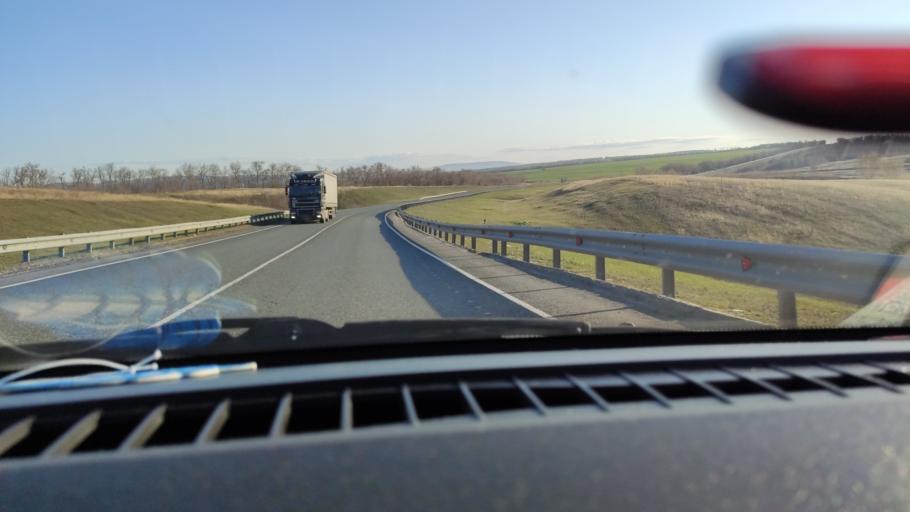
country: RU
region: Saratov
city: Balakovo
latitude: 52.1261
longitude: 47.7549
